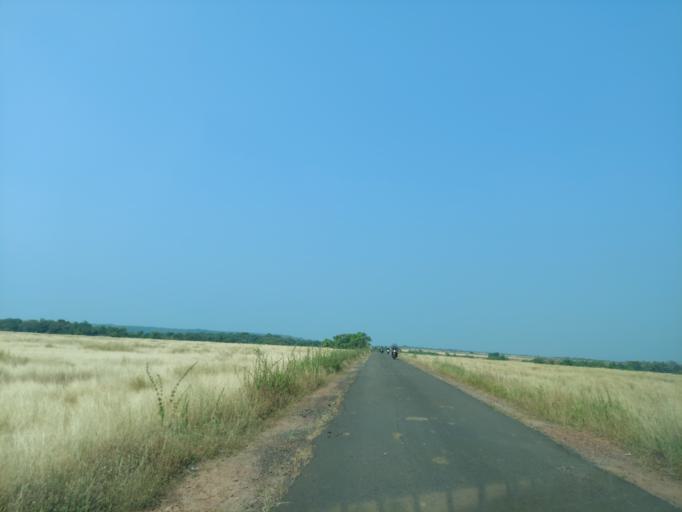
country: IN
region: Maharashtra
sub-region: Sindhudurg
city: Malvan
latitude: 15.9952
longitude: 73.5211
